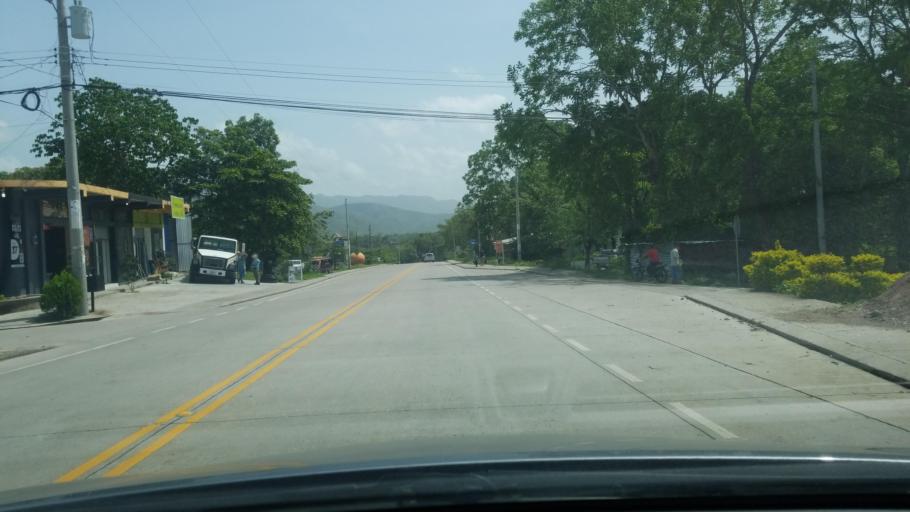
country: HN
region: Copan
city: Florida
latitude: 15.0256
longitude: -88.8323
